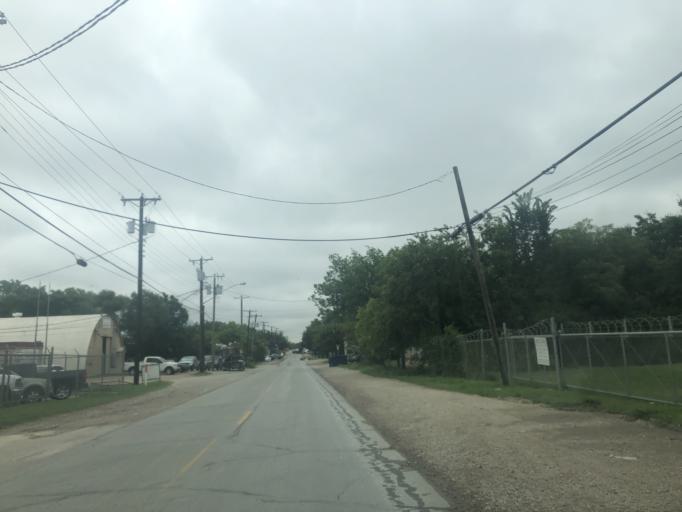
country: US
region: Texas
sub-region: Dallas County
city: Dallas
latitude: 32.7727
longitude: -96.8514
